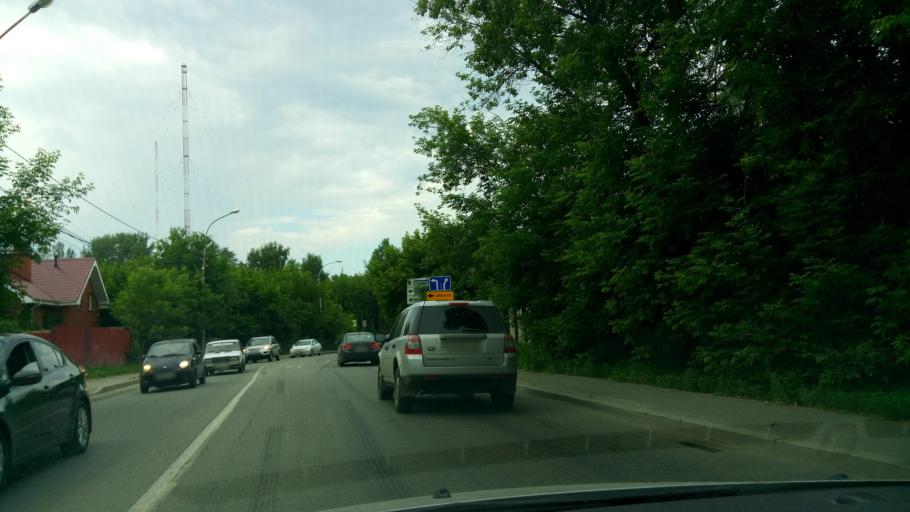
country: RU
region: Sverdlovsk
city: Yekaterinburg
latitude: 56.8808
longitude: 60.6930
